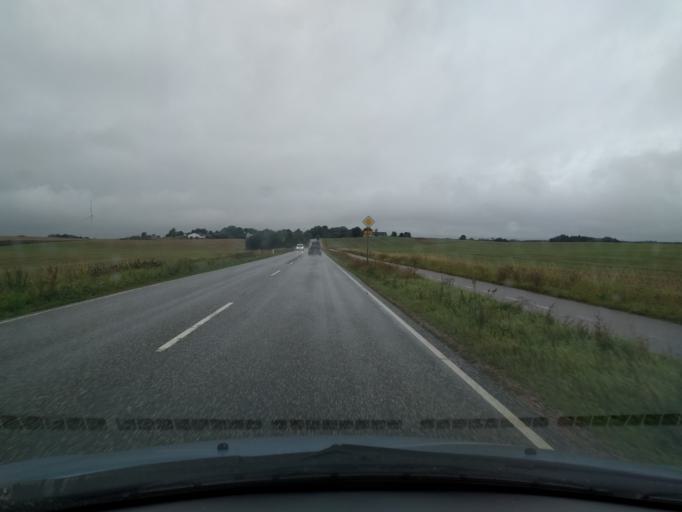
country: DK
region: Zealand
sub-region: Naestved Kommune
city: Fuglebjerg
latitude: 55.2699
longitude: 11.6410
